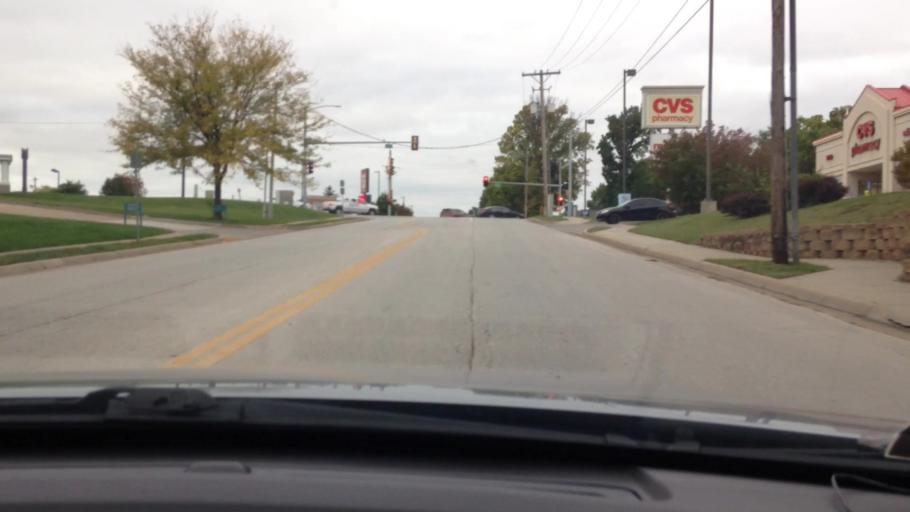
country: US
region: Kansas
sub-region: Leavenworth County
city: Leavenworth
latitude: 39.2887
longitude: -94.9055
